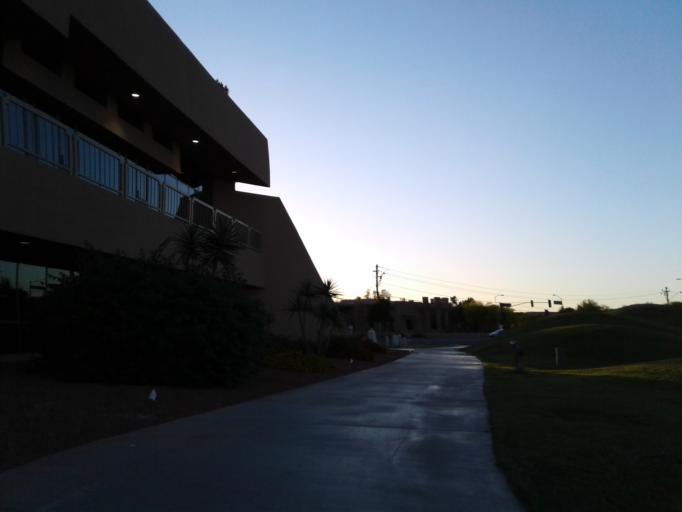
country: US
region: Arizona
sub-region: Maricopa County
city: Paradise Valley
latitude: 33.5890
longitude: -111.9771
